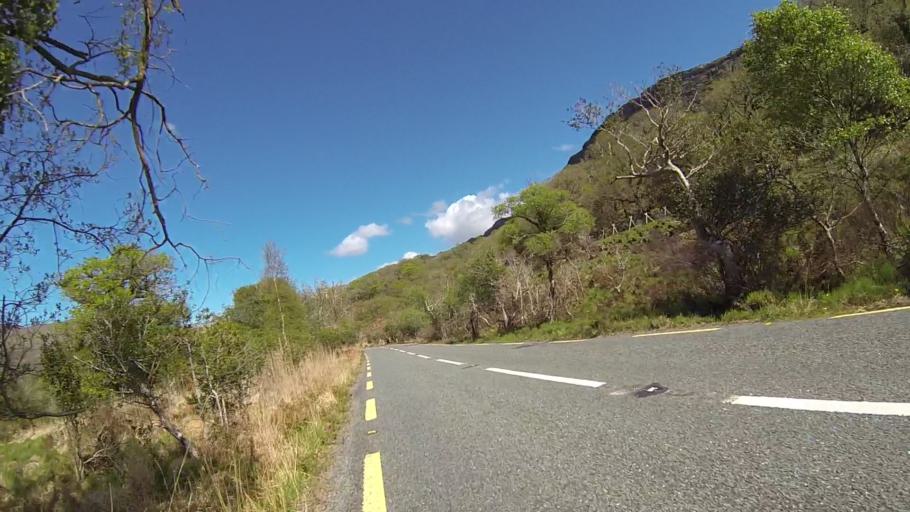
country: IE
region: Munster
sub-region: Ciarrai
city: Kenmare
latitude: 51.9752
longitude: -9.5779
